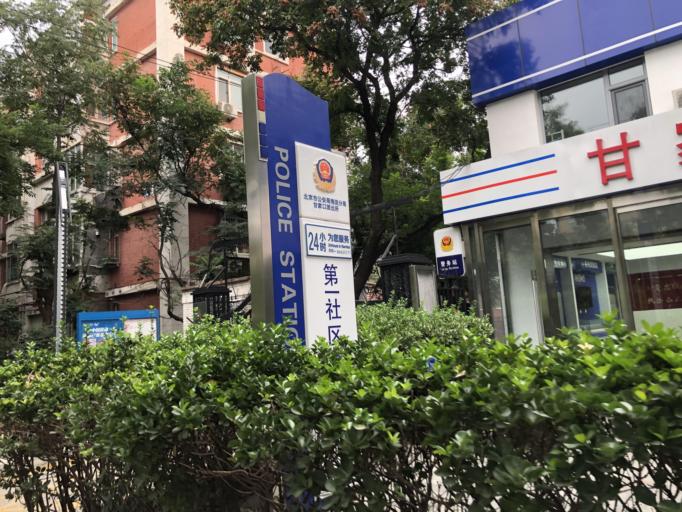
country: CN
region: Beijing
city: Jinrongjie
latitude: 39.9308
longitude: 116.3111
